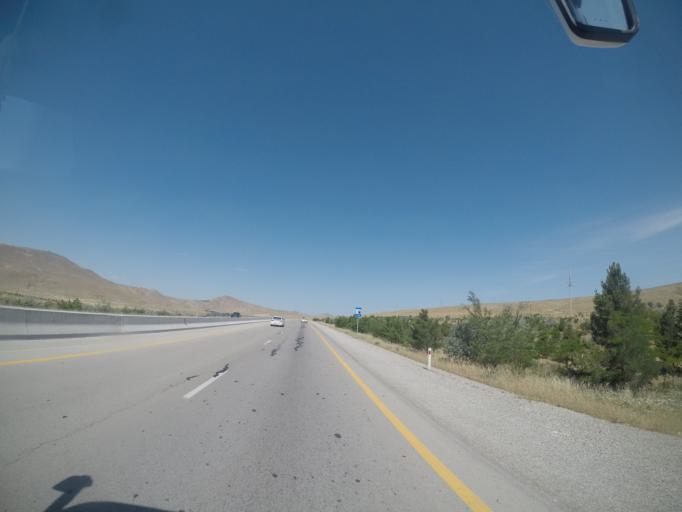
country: AZ
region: Sumqayit
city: Haci Zeynalabdin
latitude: 40.5001
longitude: 49.2880
